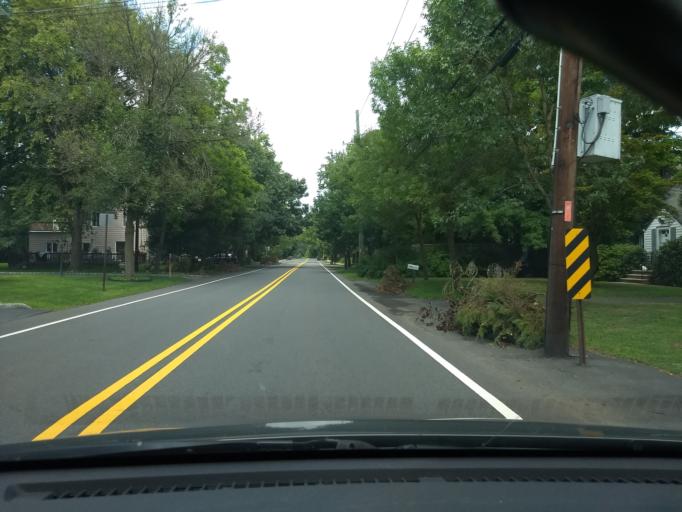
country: US
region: New Jersey
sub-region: Bergen County
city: Ho-Ho-Kus
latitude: 40.9732
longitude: -74.0902
